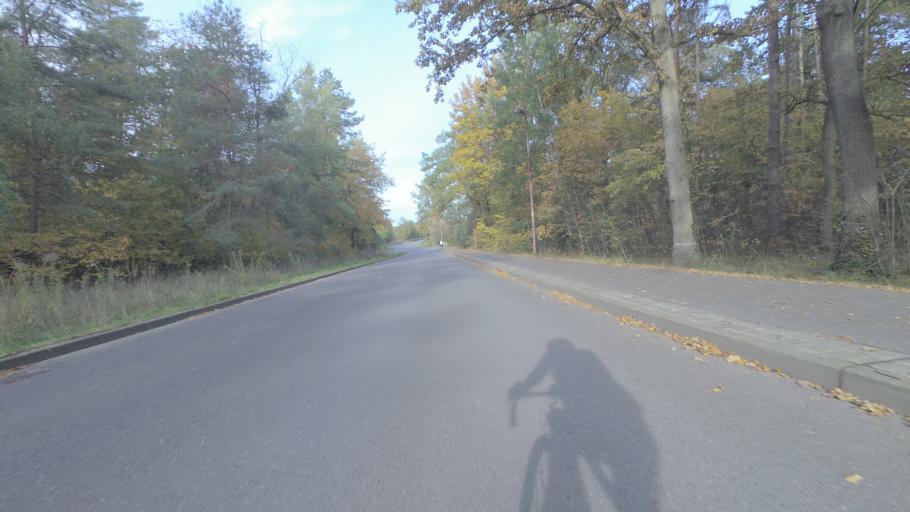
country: DE
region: Brandenburg
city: Ludwigsfelde
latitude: 52.2981
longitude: 13.2456
